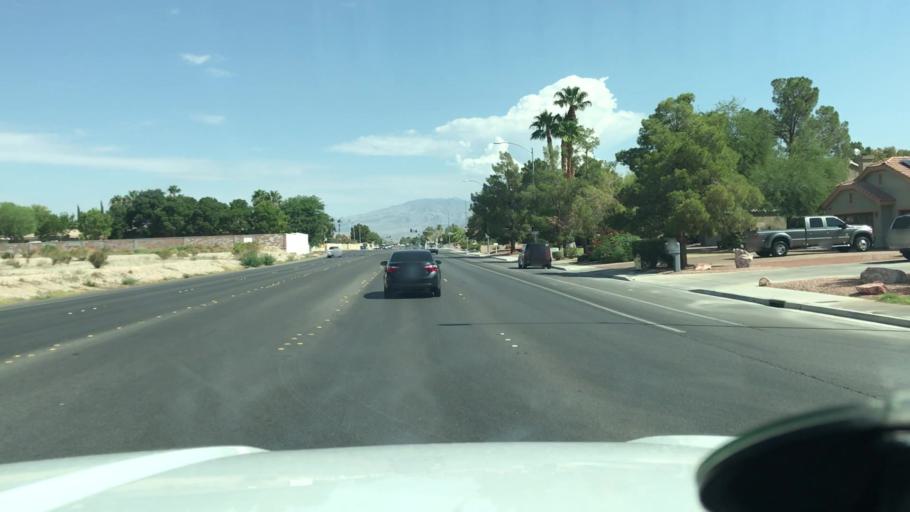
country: US
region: Nevada
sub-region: Clark County
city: Summerlin South
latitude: 36.2557
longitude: -115.2789
